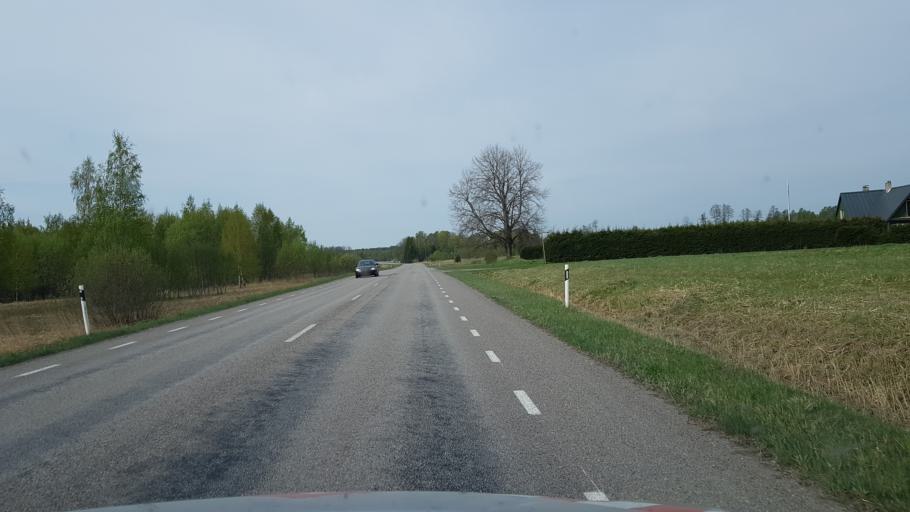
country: EE
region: Paernumaa
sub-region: Audru vald
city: Audru
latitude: 58.3976
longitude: 24.2903
